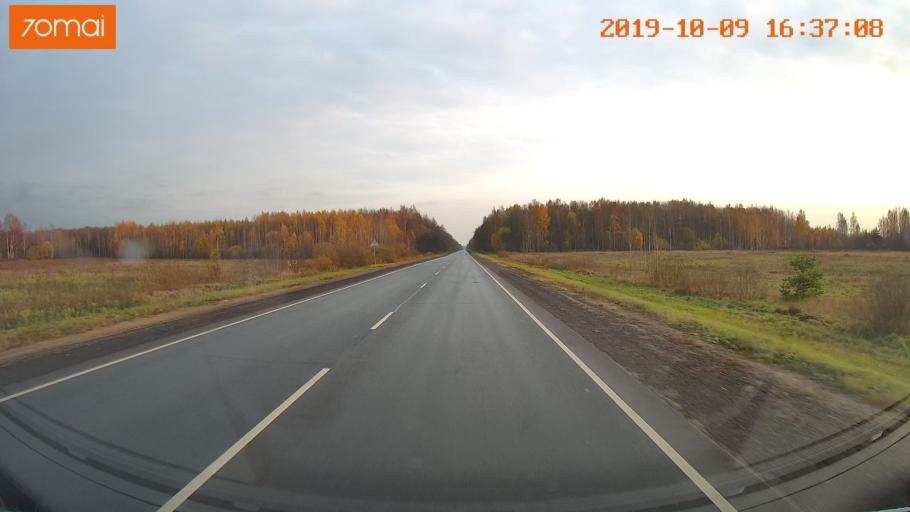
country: RU
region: Kostroma
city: Volgorechensk
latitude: 57.5314
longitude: 41.0210
